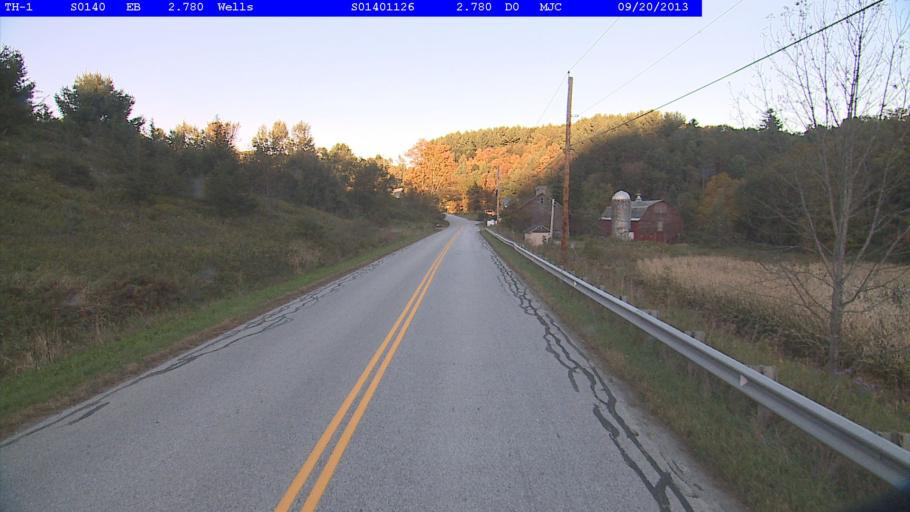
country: US
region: New York
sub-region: Washington County
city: Granville
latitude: 43.4097
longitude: -73.1529
